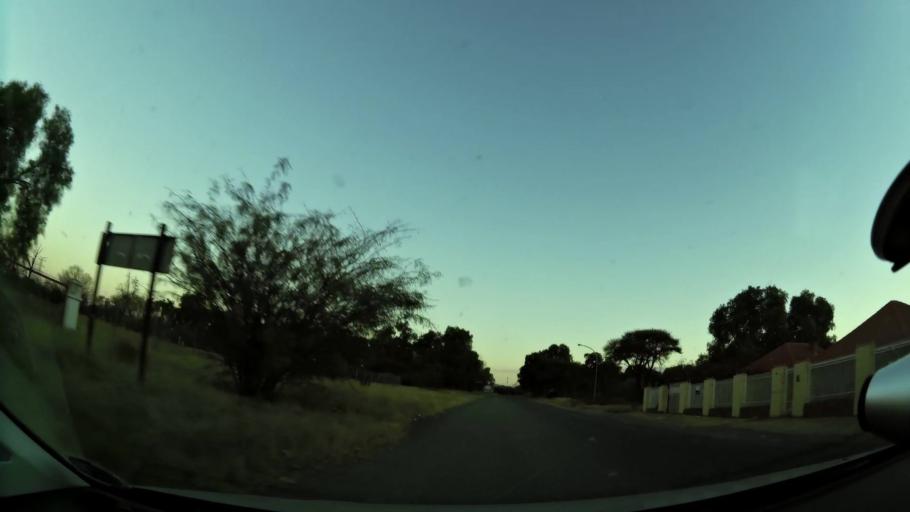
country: ZA
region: Northern Cape
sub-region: Frances Baard District Municipality
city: Kimberley
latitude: -28.7231
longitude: 24.7761
